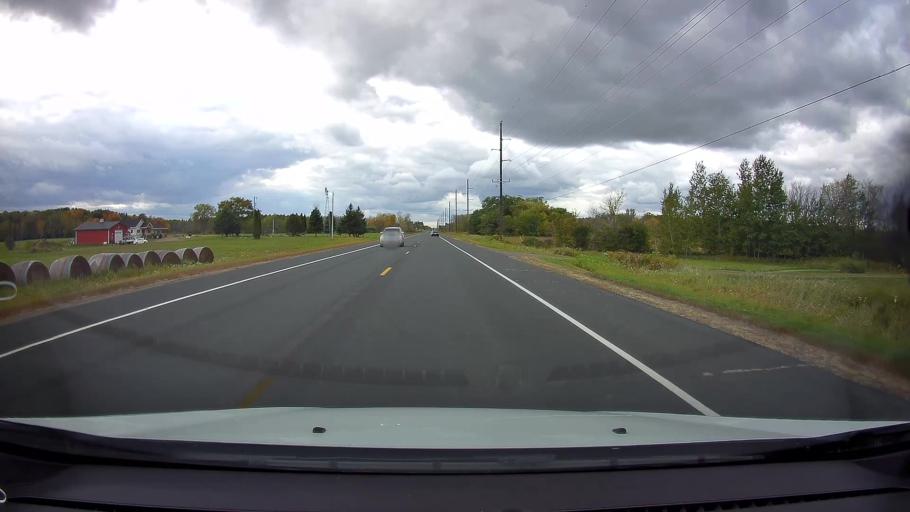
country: US
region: Minnesota
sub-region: Chisago County
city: Shafer
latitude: 45.3973
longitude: -92.7533
